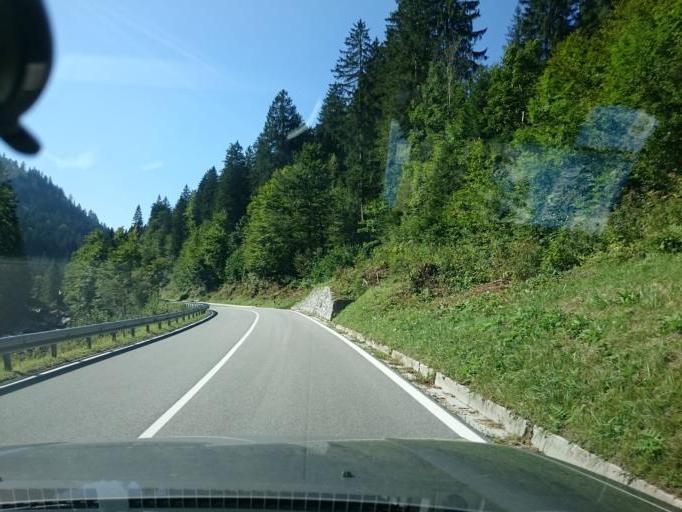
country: IT
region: Friuli Venezia Giulia
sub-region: Provincia di Udine
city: Tarvisio
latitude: 46.4763
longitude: 13.5727
